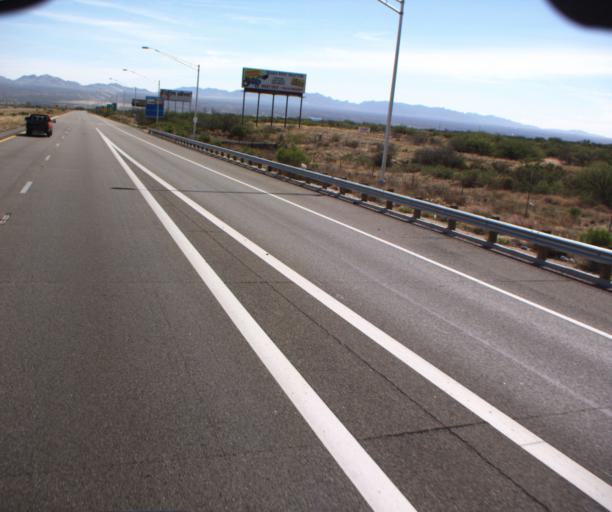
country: US
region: Arizona
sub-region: Cochise County
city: Whetstone
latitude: 31.9655
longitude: -110.3423
